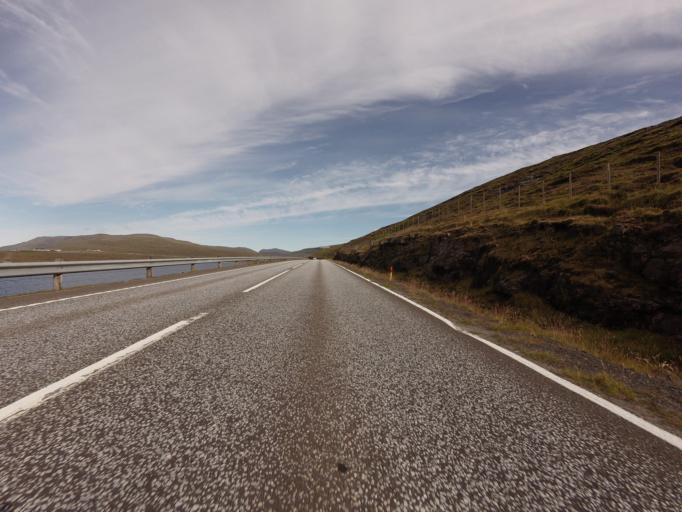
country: FO
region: Vagar
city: Midvagur
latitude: 62.0575
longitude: -7.2408
